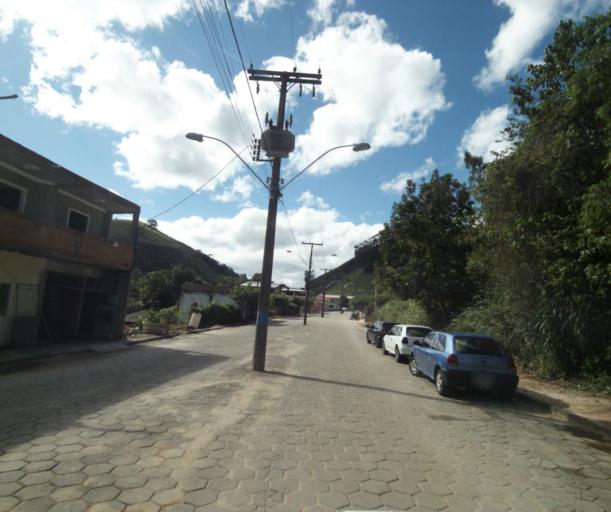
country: BR
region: Espirito Santo
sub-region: Irupi
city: Irupi
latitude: -20.5345
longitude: -41.6671
